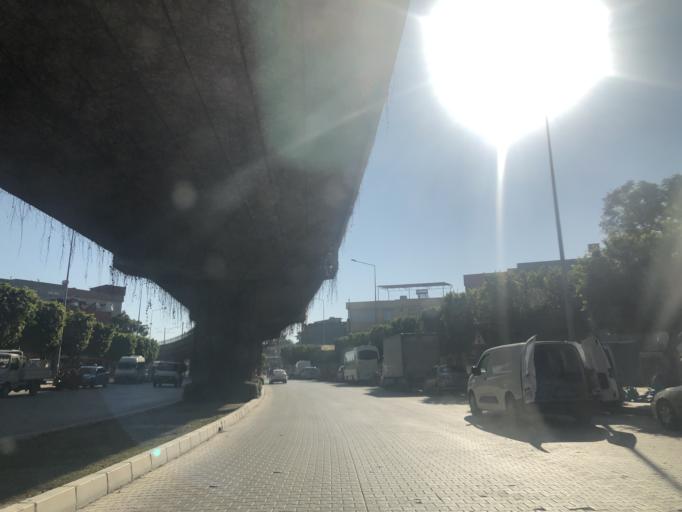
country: TR
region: Adana
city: Seyhan
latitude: 36.9803
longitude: 35.3223
